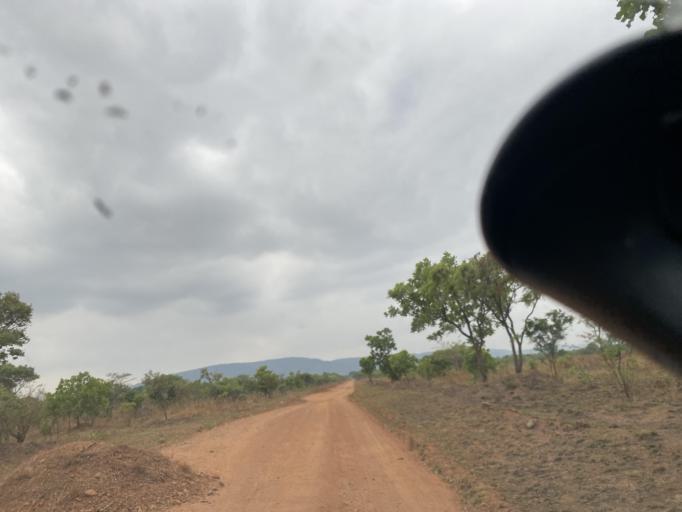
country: ZM
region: Lusaka
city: Chongwe
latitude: -15.2123
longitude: 28.7556
